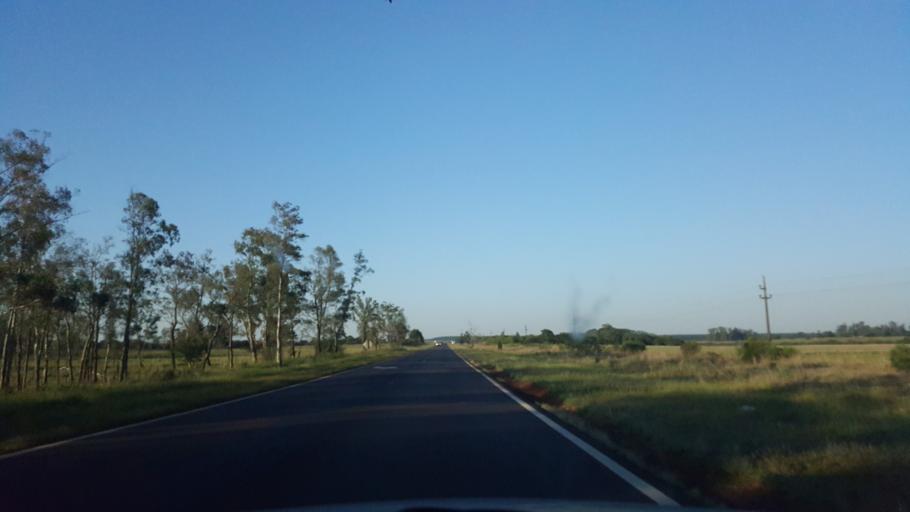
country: AR
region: Corrientes
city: Santo Tome
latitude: -28.4854
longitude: -56.1151
